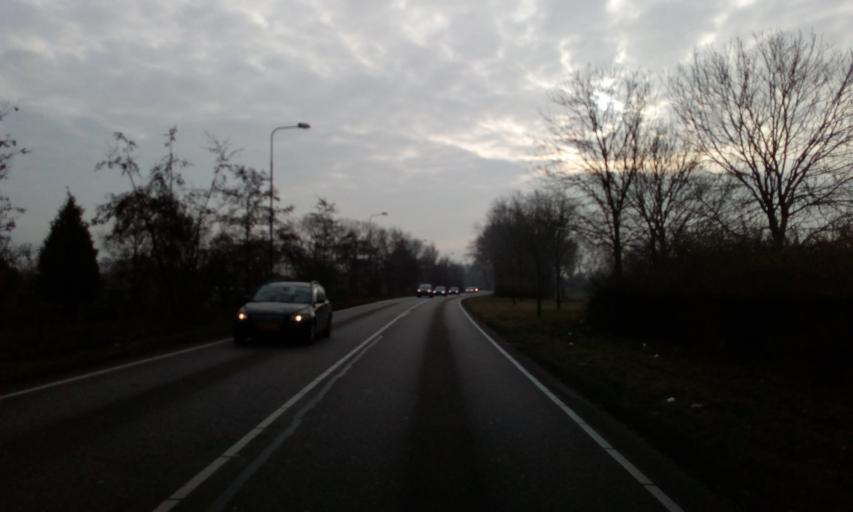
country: NL
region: North Holland
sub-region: Gemeente Naarden
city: Naarden
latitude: 52.2970
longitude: 5.1443
